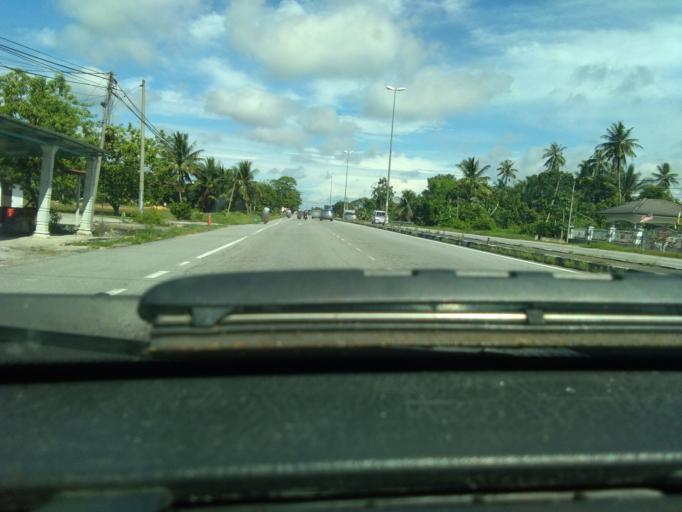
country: MY
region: Perak
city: Bagan Serai
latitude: 5.0019
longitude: 100.5507
